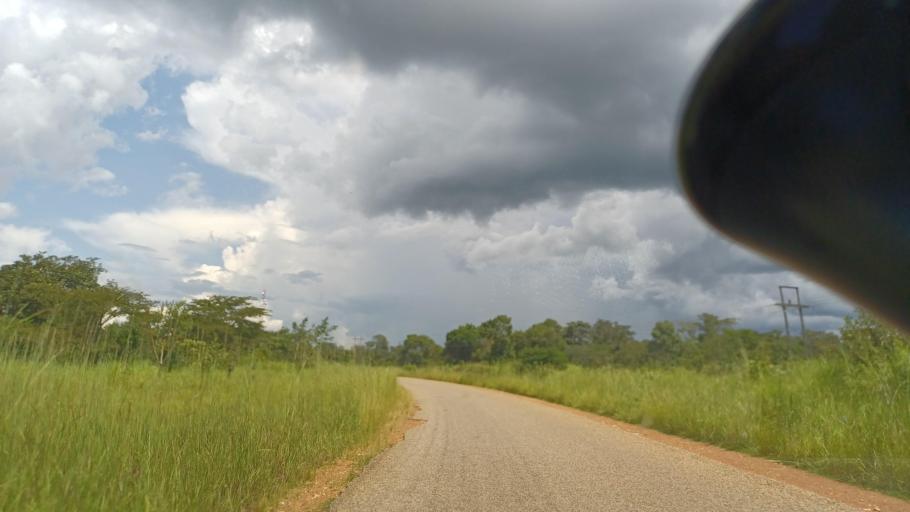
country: ZM
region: North-Western
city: Kasempa
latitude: -12.7804
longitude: 26.0089
